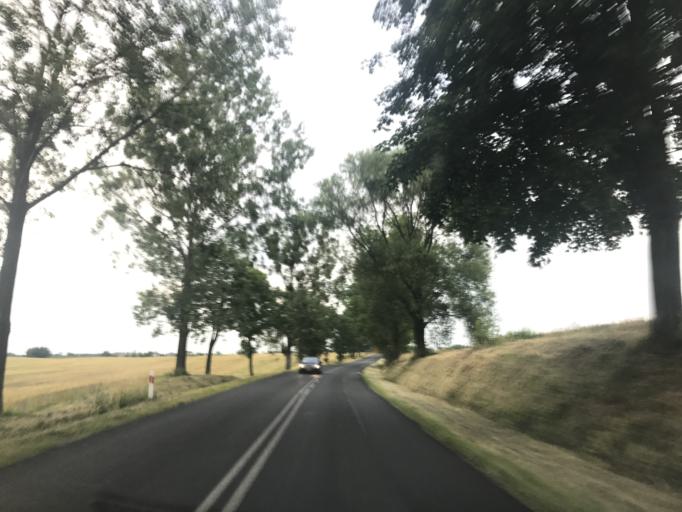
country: PL
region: Kujawsko-Pomorskie
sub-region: Powiat rypinski
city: Rogowo
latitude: 53.0296
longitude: 19.3603
